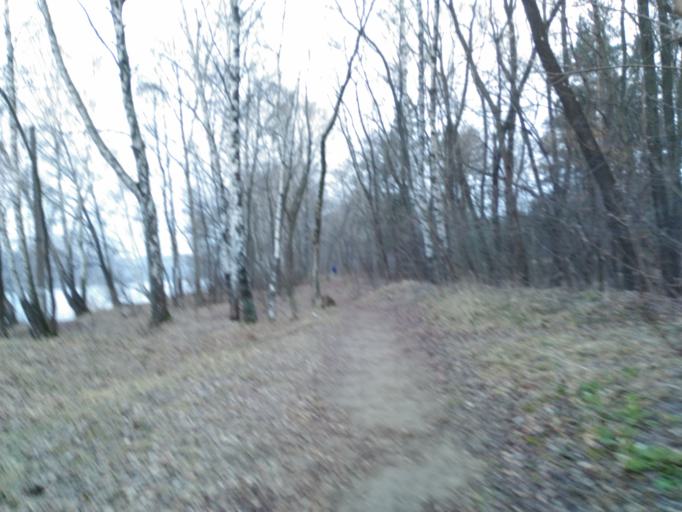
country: RU
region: Moscow
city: Shchukino
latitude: 55.7758
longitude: 37.4224
